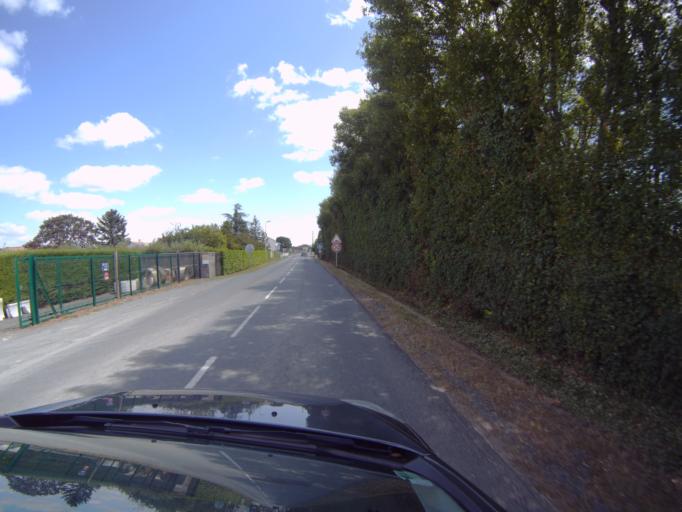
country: FR
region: Poitou-Charentes
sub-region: Departement de la Charente-Maritime
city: Saint-Jean-de-Liversay
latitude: 46.2660
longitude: -0.8764
